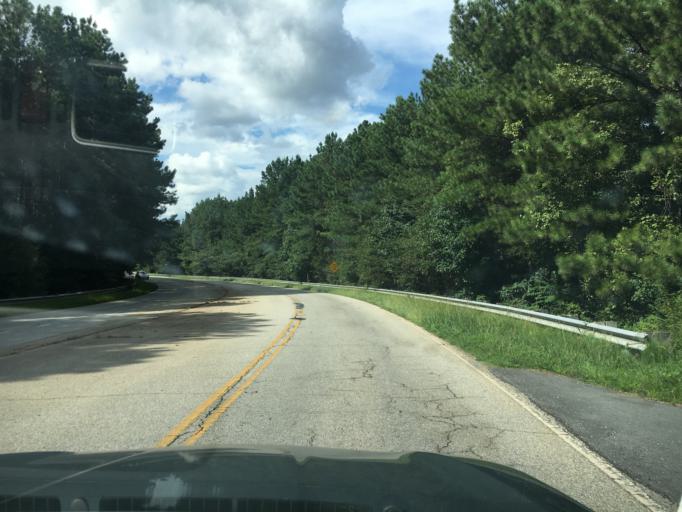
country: US
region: South Carolina
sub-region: Spartanburg County
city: Southern Shops
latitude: 34.9982
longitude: -81.9885
